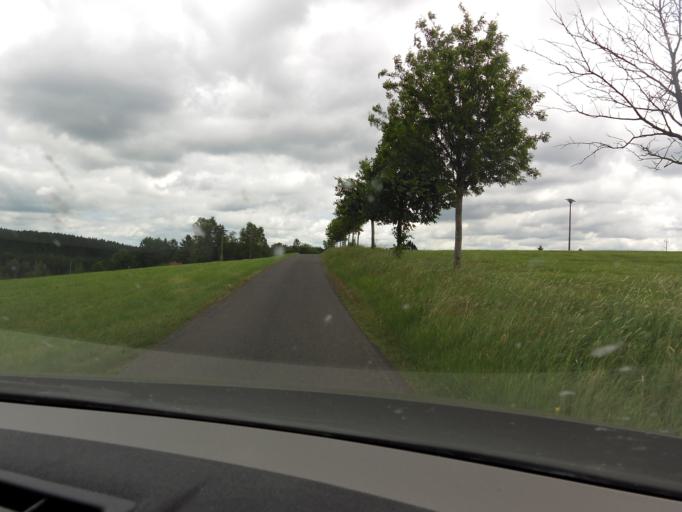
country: DE
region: Thuringia
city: Finsterbergen
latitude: 50.8356
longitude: 10.5811
